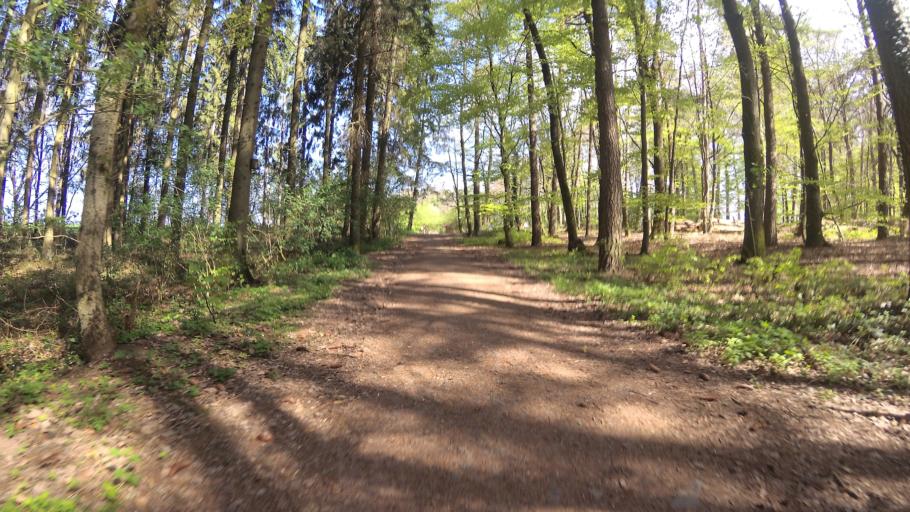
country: DE
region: Saarland
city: Mainzweiler
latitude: 49.4660
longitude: 7.1086
